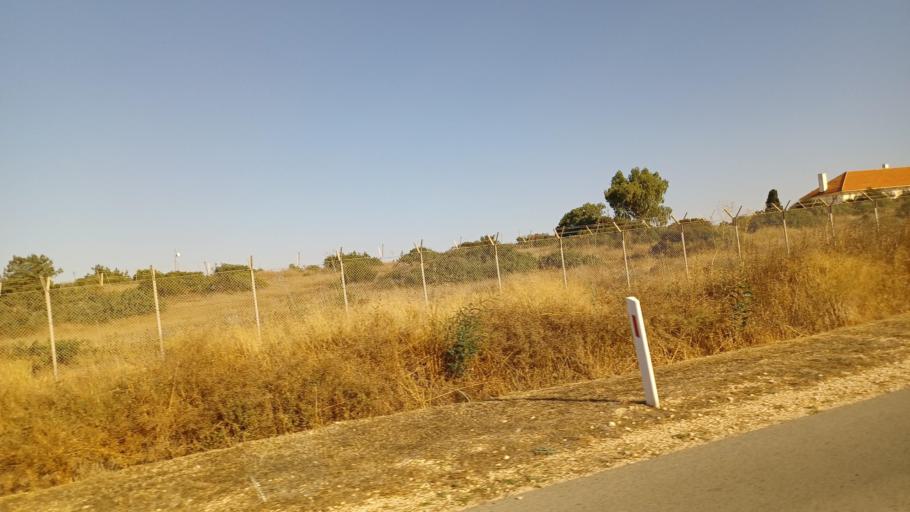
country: CY
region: Larnaka
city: Xylotymbou
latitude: 34.9947
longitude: 33.7426
